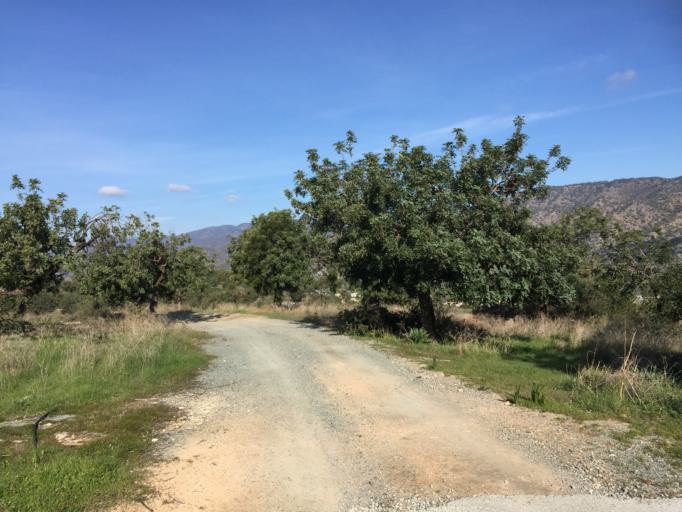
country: CY
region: Larnaka
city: Agios Tychon
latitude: 34.7457
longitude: 33.1284
